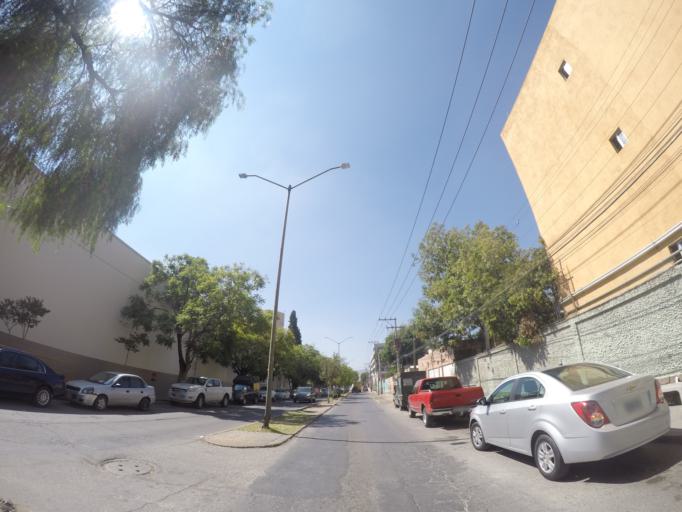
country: MX
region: San Luis Potosi
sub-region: San Luis Potosi
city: San Luis Potosi
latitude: 22.1466
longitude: -101.0142
